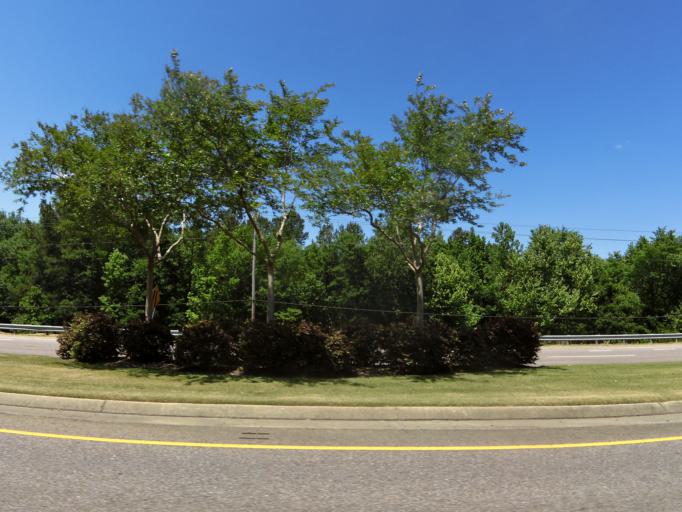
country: US
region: South Carolina
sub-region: Aiken County
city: North Augusta
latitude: 33.4850
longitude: -81.9396
